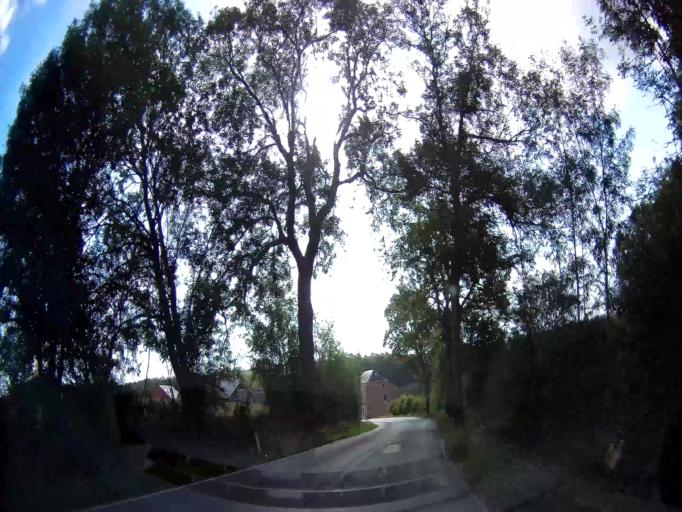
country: BE
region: Wallonia
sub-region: Province du Luxembourg
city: Wellin
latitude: 50.1701
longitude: 5.1285
